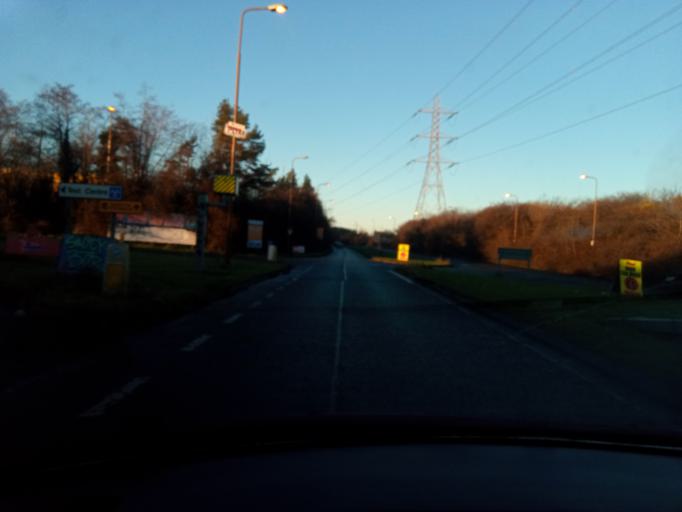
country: GB
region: Scotland
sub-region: West Lothian
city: Seafield
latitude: 55.9494
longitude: -3.1095
